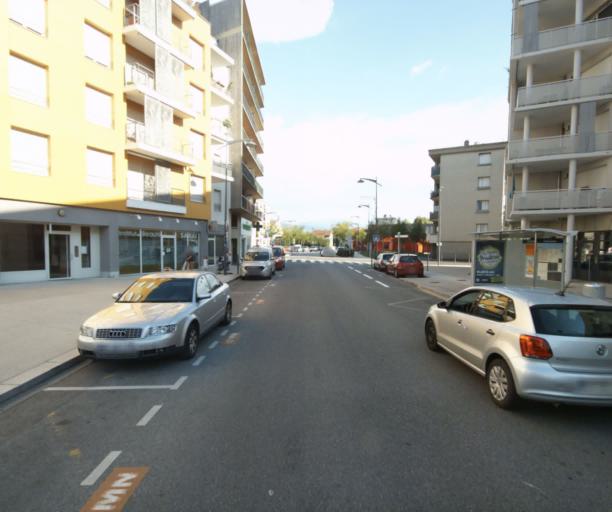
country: FR
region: Rhone-Alpes
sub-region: Departement de l'Isere
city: Fontaine
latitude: 45.1980
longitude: 5.6930
